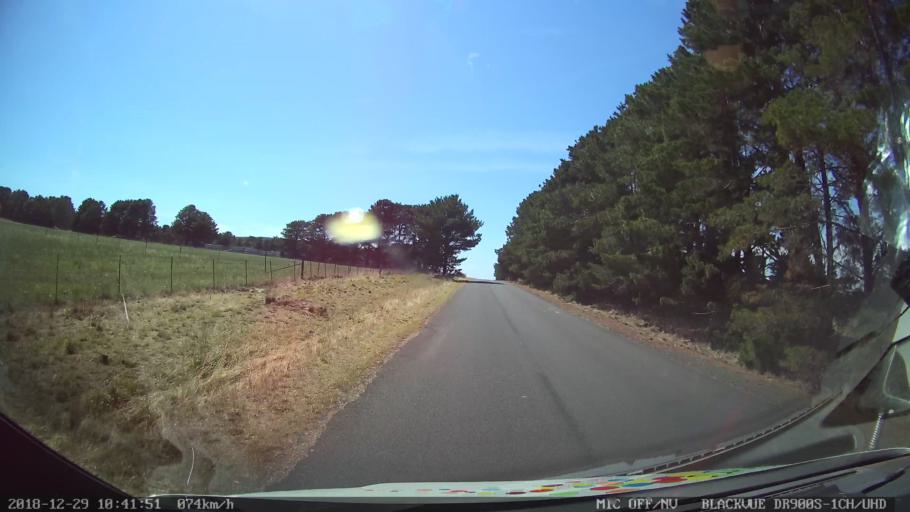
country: AU
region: New South Wales
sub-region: Palerang
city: Bungendore
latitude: -35.0289
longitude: 149.5241
